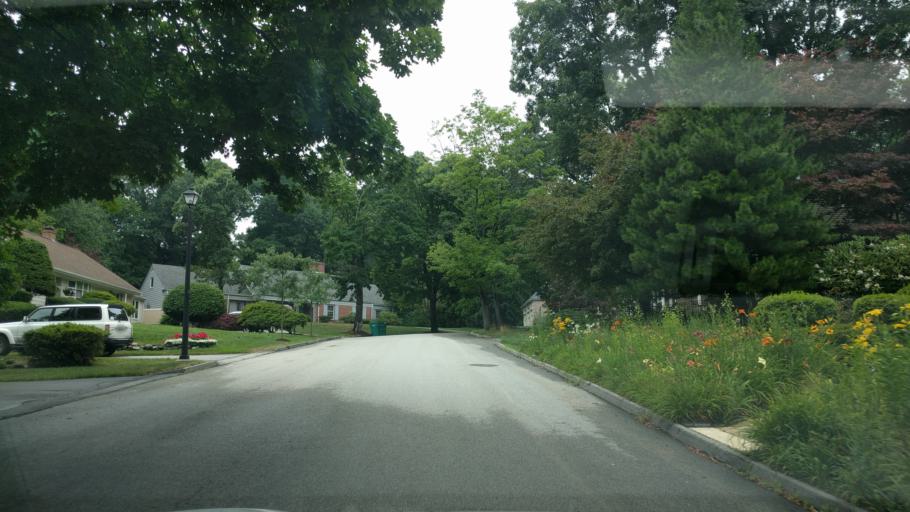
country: US
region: Massachusetts
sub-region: Worcester County
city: Worcester
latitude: 42.2893
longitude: -71.8209
